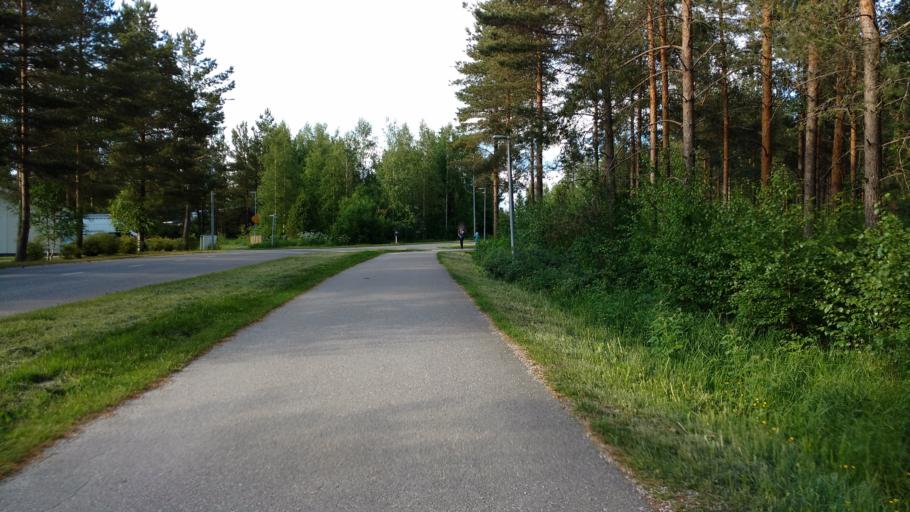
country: FI
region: Varsinais-Suomi
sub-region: Salo
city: Salo
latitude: 60.3939
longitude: 23.1875
